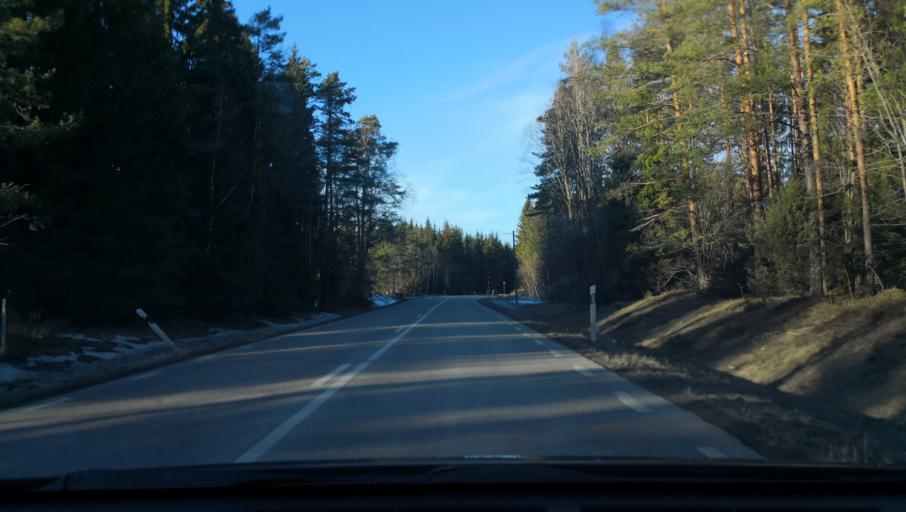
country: SE
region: Uppsala
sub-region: Osthammars Kommun
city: Gimo
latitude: 60.2095
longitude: 18.1921
